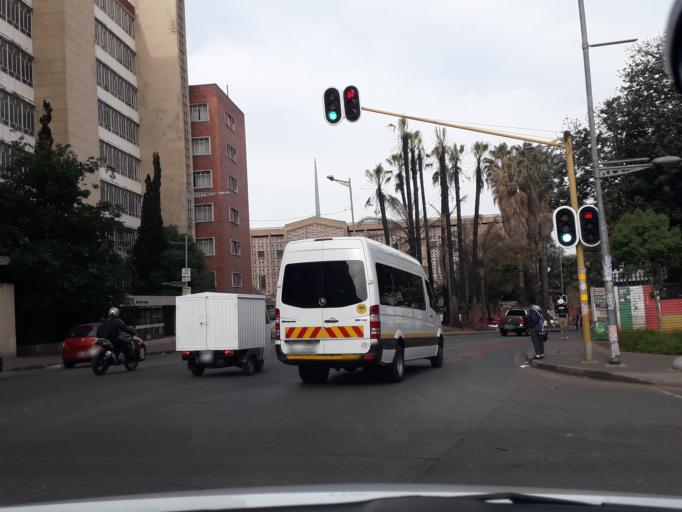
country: ZA
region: Gauteng
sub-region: City of Johannesburg Metropolitan Municipality
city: Johannesburg
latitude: -26.1935
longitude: 28.0505
